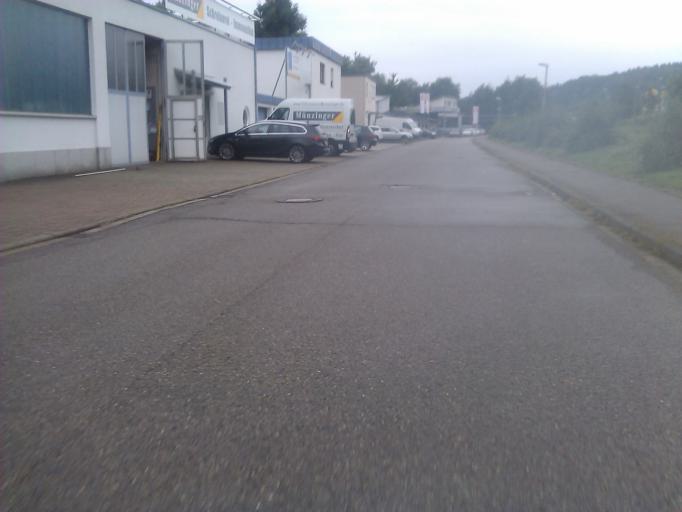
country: DE
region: Baden-Wuerttemberg
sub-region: Regierungsbezirk Stuttgart
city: Neckartenzlingen
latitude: 48.5884
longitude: 9.2298
